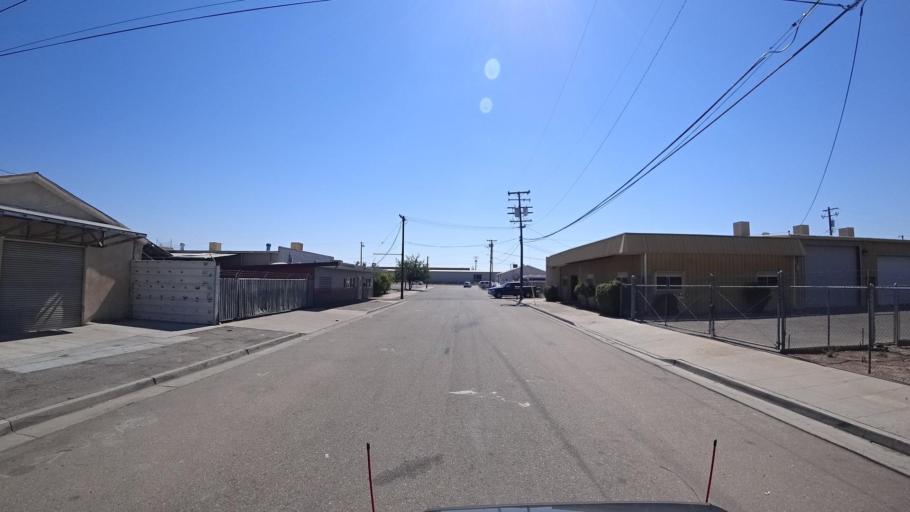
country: US
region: California
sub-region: Fresno County
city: Fresno
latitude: 36.7568
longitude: -119.7468
